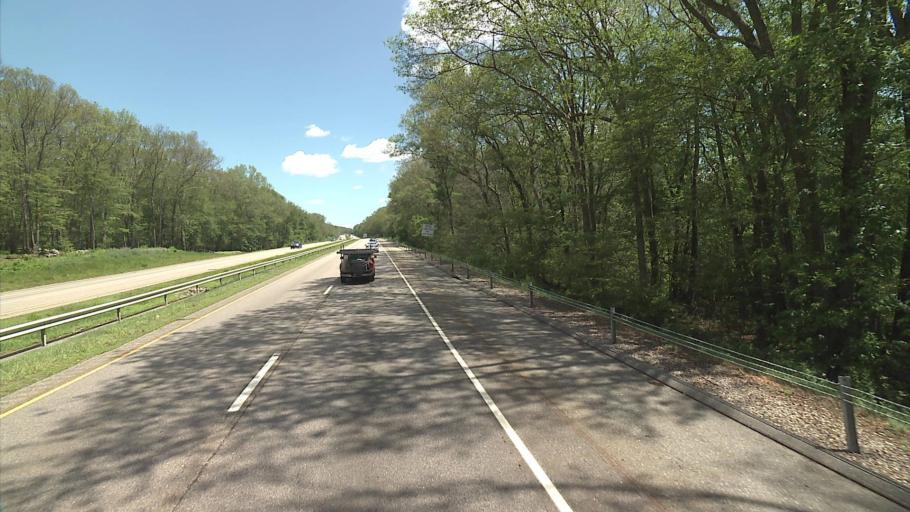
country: US
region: Connecticut
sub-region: New London County
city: Niantic
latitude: 41.3786
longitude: -72.1895
